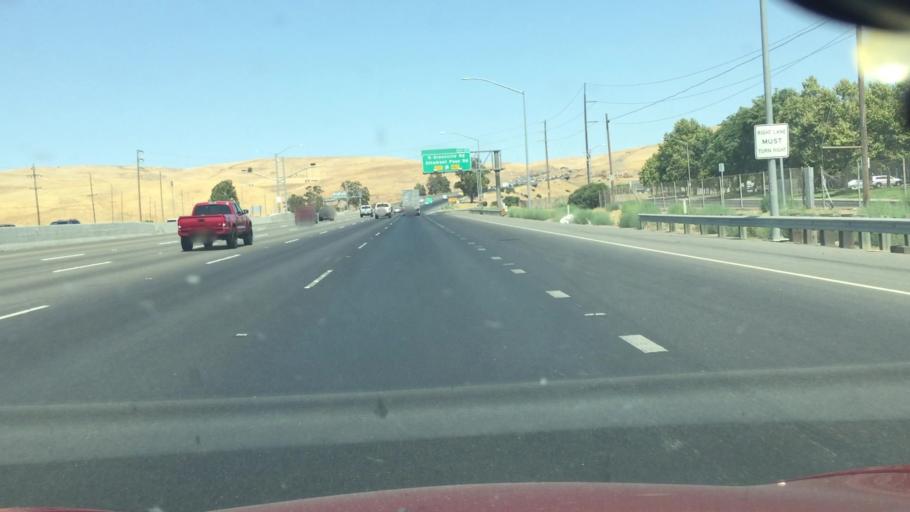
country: US
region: California
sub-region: Alameda County
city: Livermore
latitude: 37.7162
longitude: -121.7098
